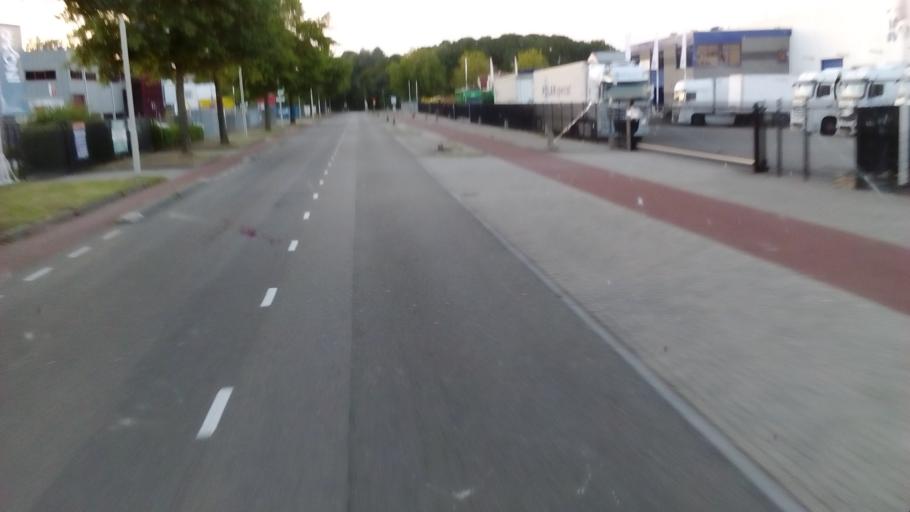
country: NL
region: Gelderland
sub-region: Gemeente Nijmegen
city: Lindenholt
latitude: 51.8447
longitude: 5.8013
